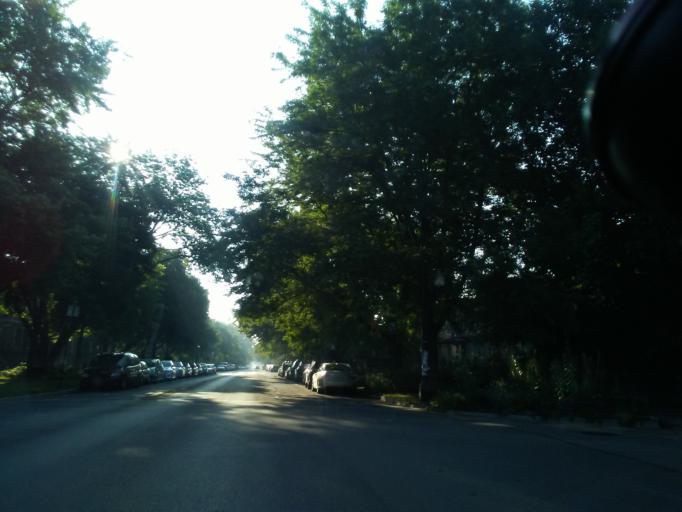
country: US
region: Illinois
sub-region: Cook County
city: Oak Park
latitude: 41.9281
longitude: -87.7257
